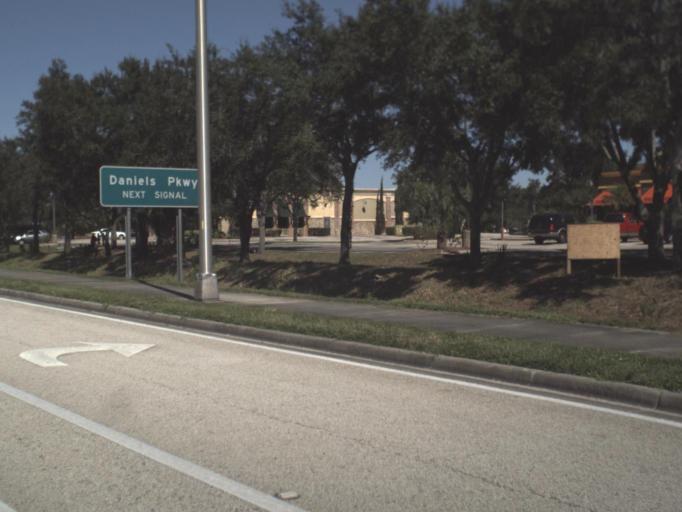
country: US
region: Florida
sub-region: Lee County
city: Villas
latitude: 26.5428
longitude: -81.8713
